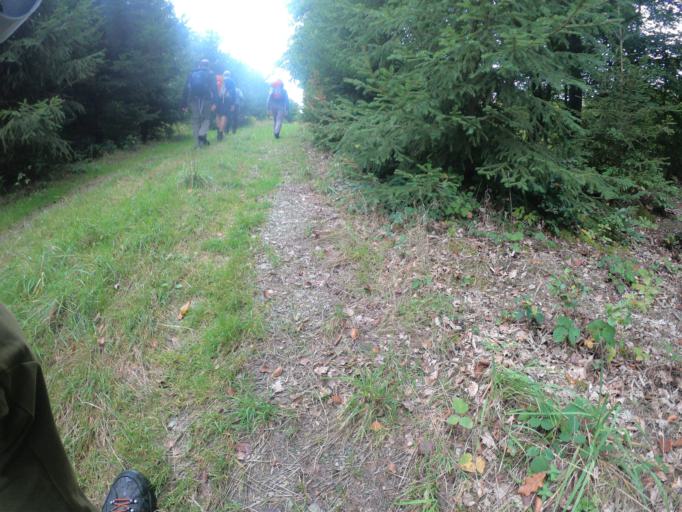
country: DE
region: Hesse
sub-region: Regierungsbezirk Darmstadt
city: Waldems
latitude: 50.2023
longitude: 8.3233
